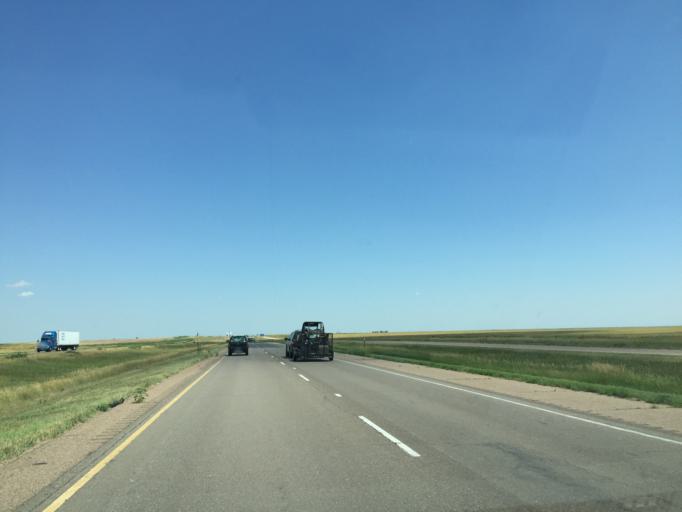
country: US
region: Colorado
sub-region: Lincoln County
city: Hugo
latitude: 39.2813
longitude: -103.3341
